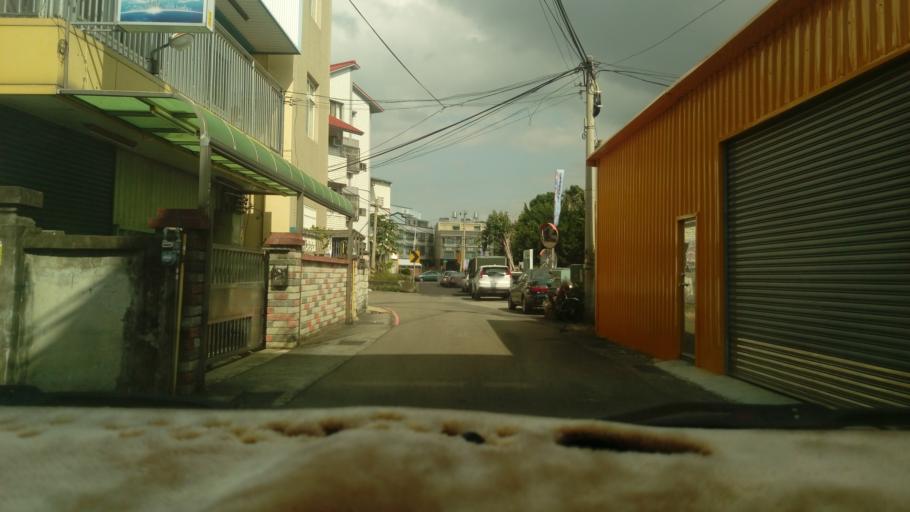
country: TW
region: Taiwan
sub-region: Miaoli
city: Miaoli
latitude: 24.5648
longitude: 120.8273
